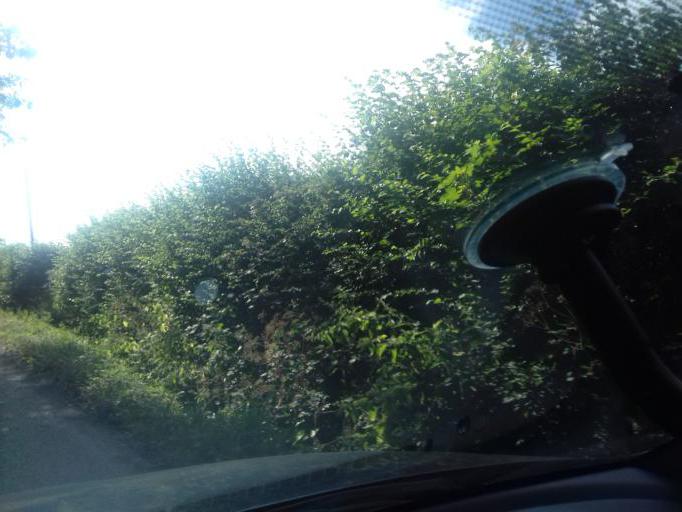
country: IE
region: Leinster
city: Hartstown
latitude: 53.4375
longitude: -6.4342
